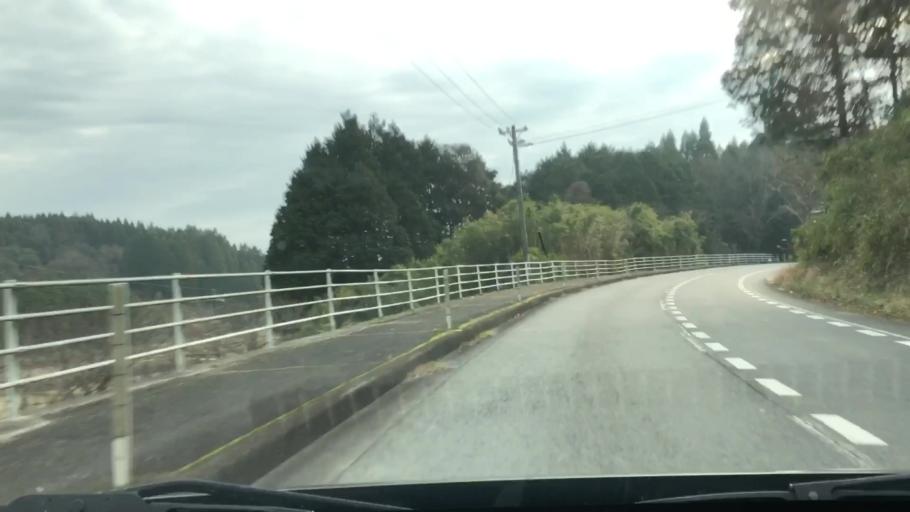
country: JP
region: Oita
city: Takedamachi
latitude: 32.9783
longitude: 131.5580
